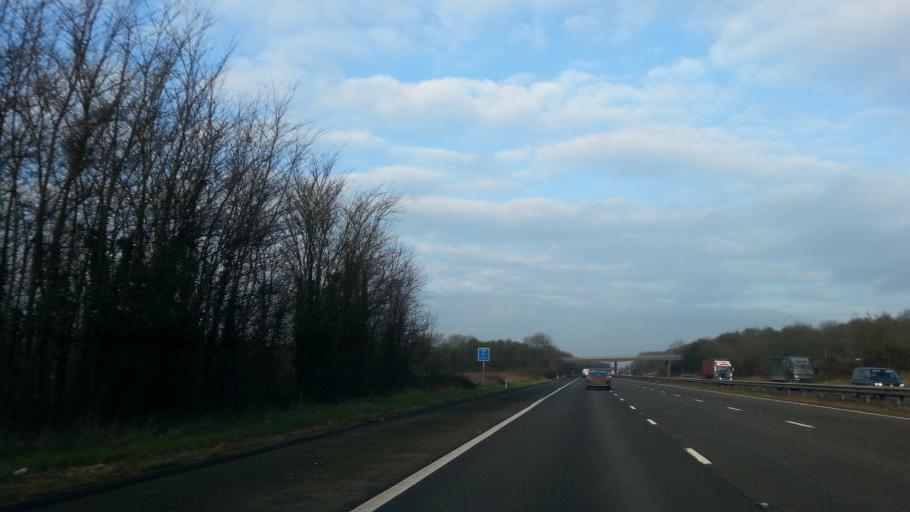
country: GB
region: England
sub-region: Gloucestershire
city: Dursley
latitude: 51.6949
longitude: -2.3945
